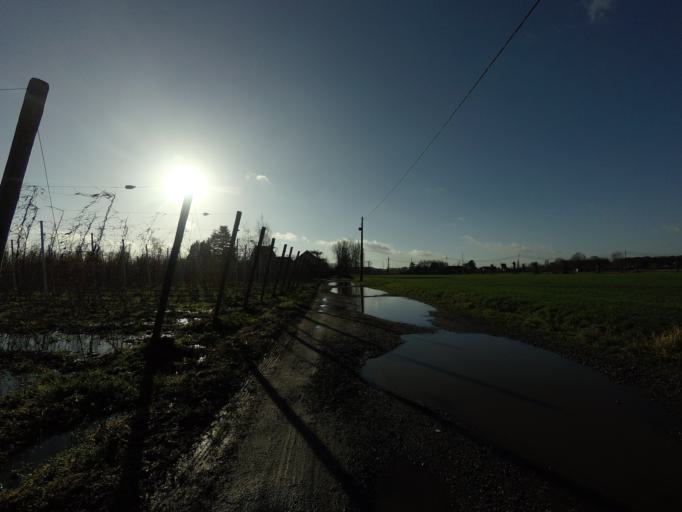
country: BE
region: Flanders
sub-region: Provincie Antwerpen
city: Lint
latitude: 51.1343
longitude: 4.5330
